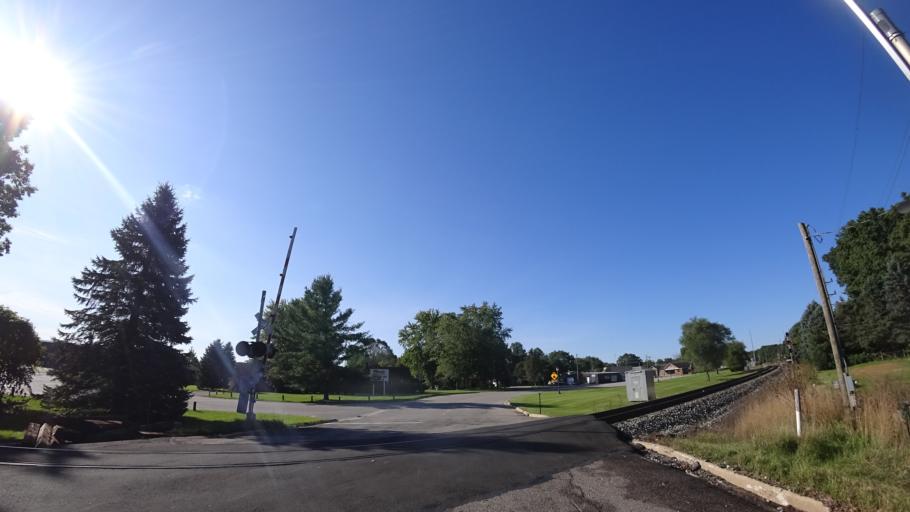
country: US
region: Michigan
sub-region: Berrien County
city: Lake Michigan Beach
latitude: 42.1841
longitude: -86.3816
